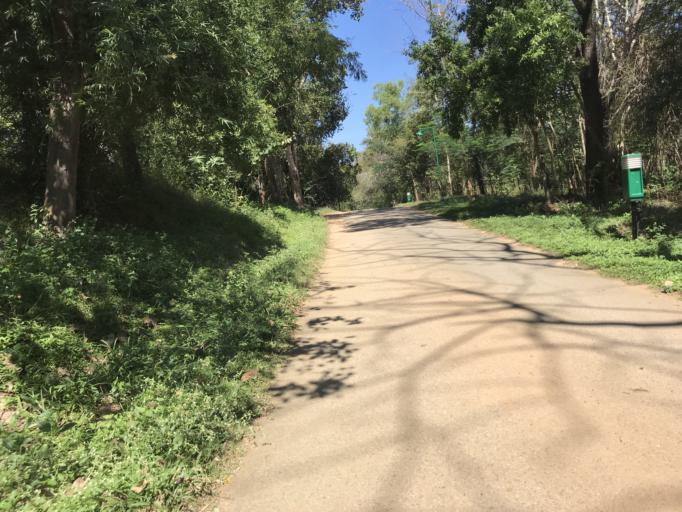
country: IN
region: Karnataka
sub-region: Mysore
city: Sargur
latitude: 11.9395
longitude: 76.2702
